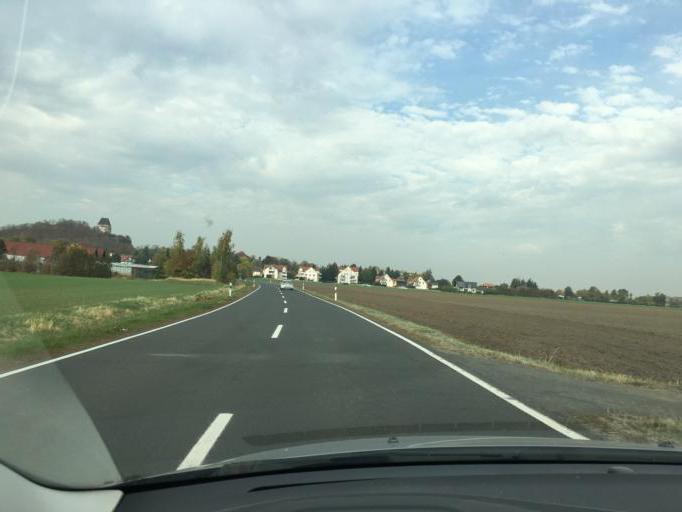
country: DE
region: Saxony-Anhalt
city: Landsberg
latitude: 51.5191
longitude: 12.1690
